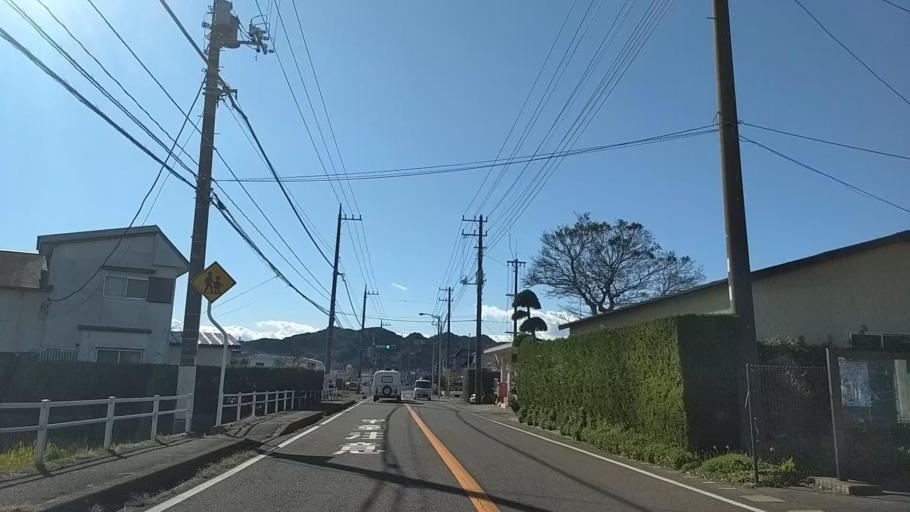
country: JP
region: Chiba
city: Tateyama
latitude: 34.9338
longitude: 139.8396
